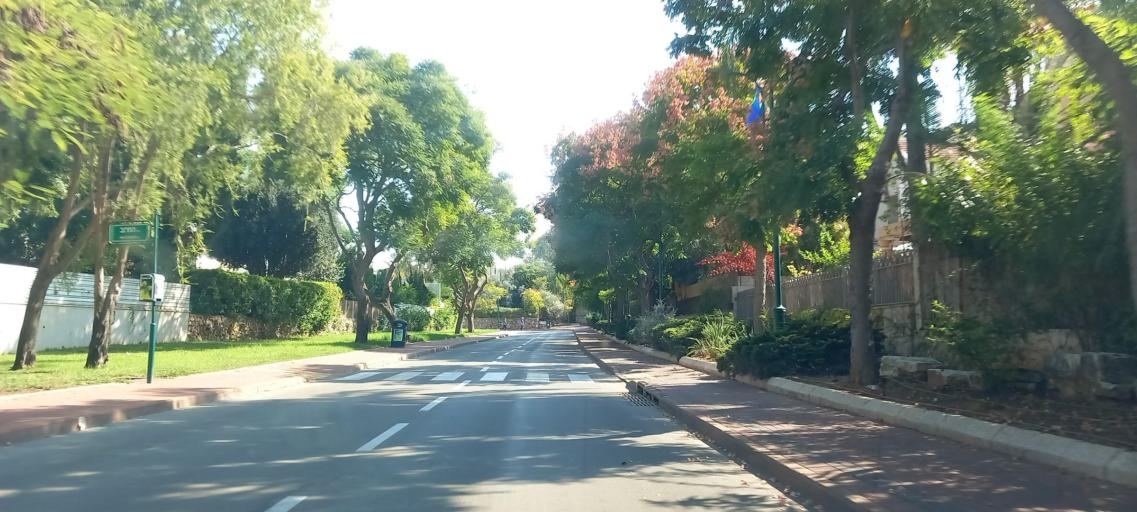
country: IL
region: Tel Aviv
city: Or Yehuda
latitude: 32.0436
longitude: 34.8352
